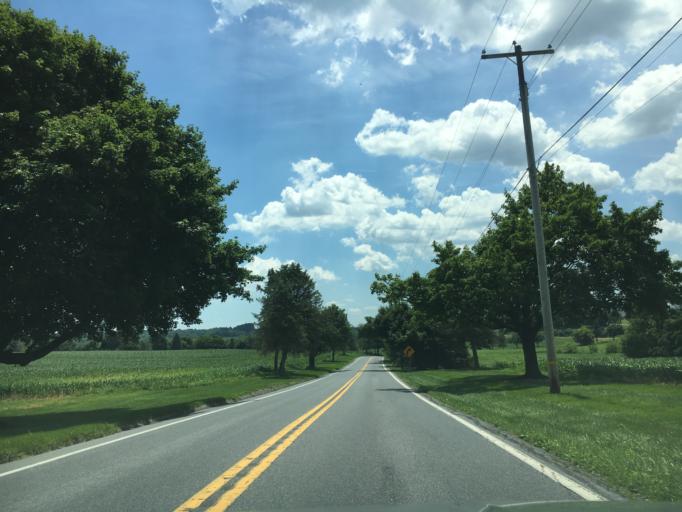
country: US
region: Pennsylvania
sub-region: Lehigh County
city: Schnecksville
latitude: 40.6390
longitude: -75.5773
